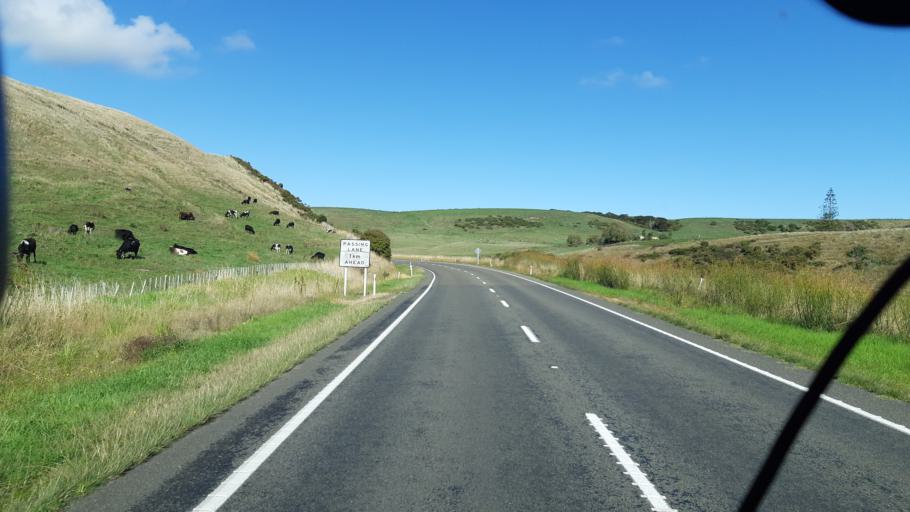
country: NZ
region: Manawatu-Wanganui
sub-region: Wanganui District
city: Wanganui
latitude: -40.0139
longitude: 175.1728
